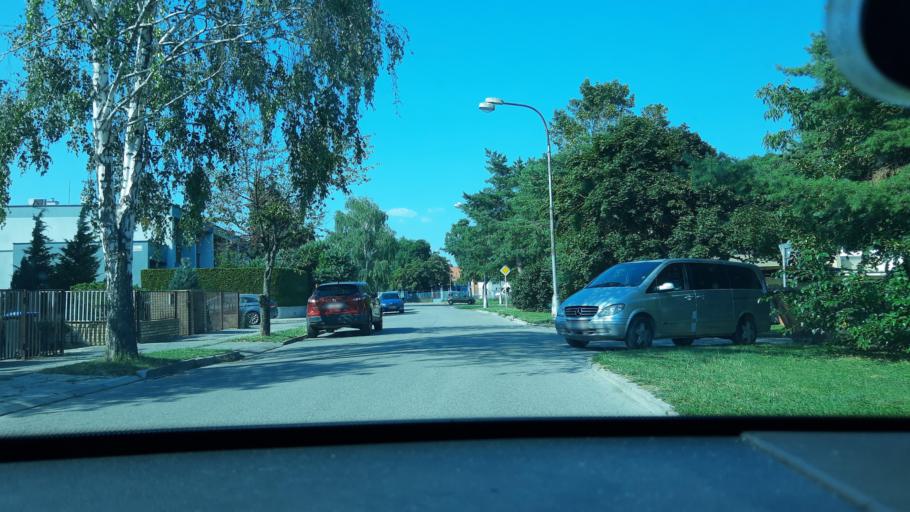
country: SK
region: Trnavsky
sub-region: Okres Trnava
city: Piestany
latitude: 48.6019
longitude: 17.8371
